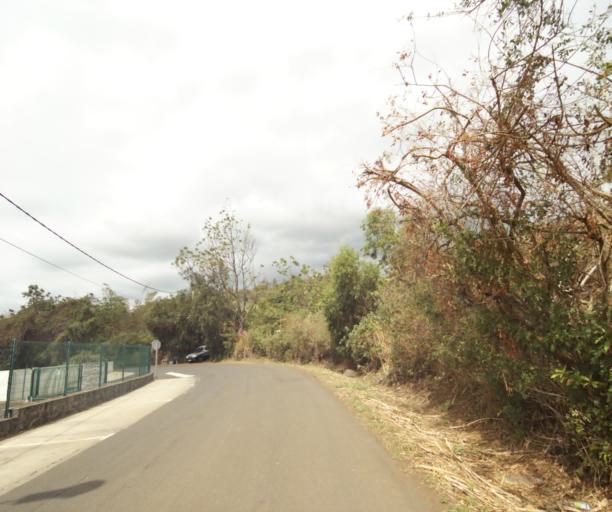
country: RE
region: Reunion
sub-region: Reunion
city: Saint-Paul
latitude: -21.0364
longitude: 55.2895
